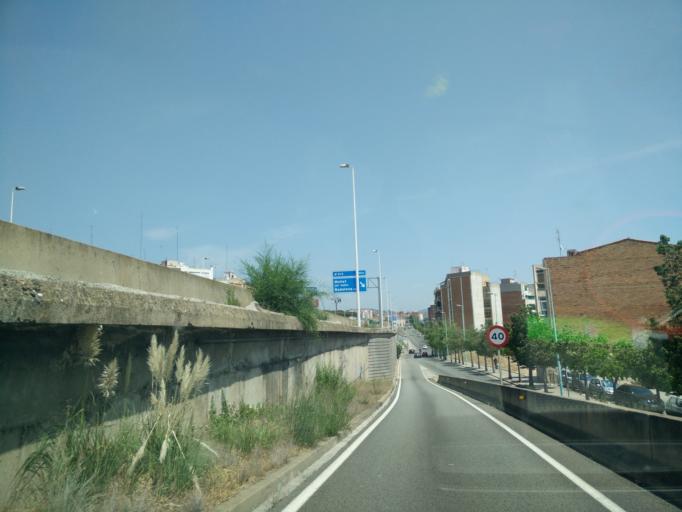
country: ES
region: Catalonia
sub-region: Provincia de Barcelona
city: Badalona
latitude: 41.4495
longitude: 2.2378
